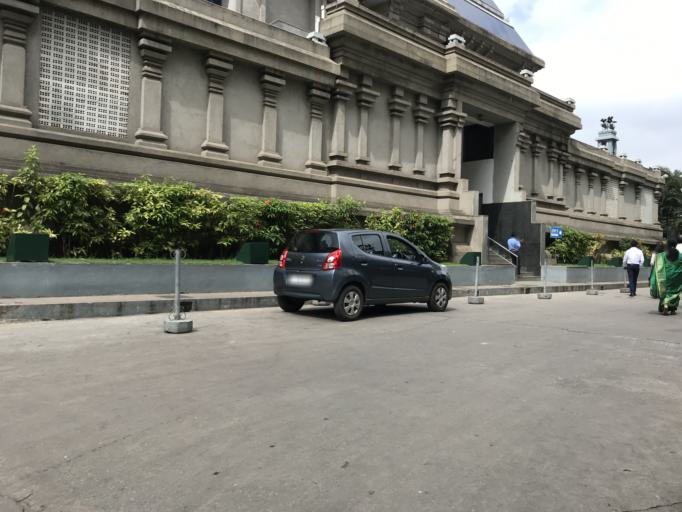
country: IN
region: Karnataka
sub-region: Bangalore Urban
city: Bangalore
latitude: 13.0095
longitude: 77.5516
